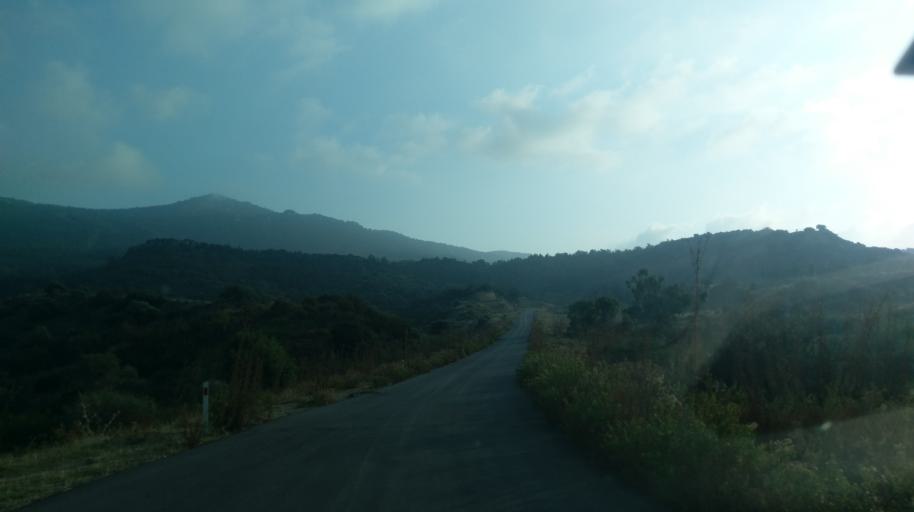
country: CY
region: Ammochostos
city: Trikomo
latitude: 35.4212
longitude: 33.9080
